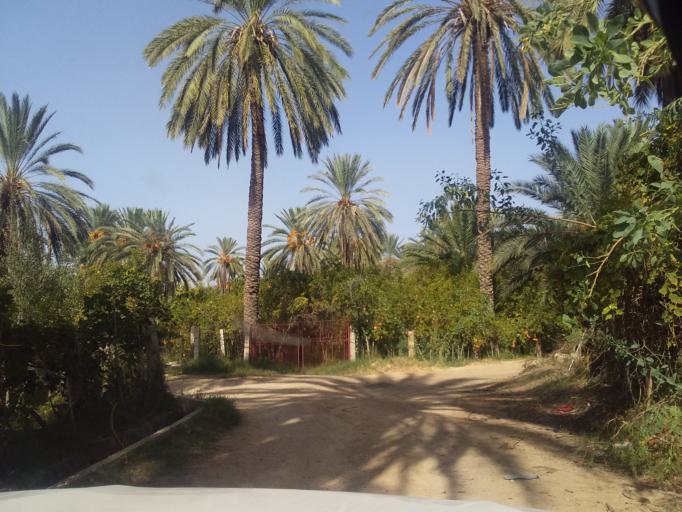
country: TN
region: Qabis
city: Gabes
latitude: 33.6269
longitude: 10.2858
